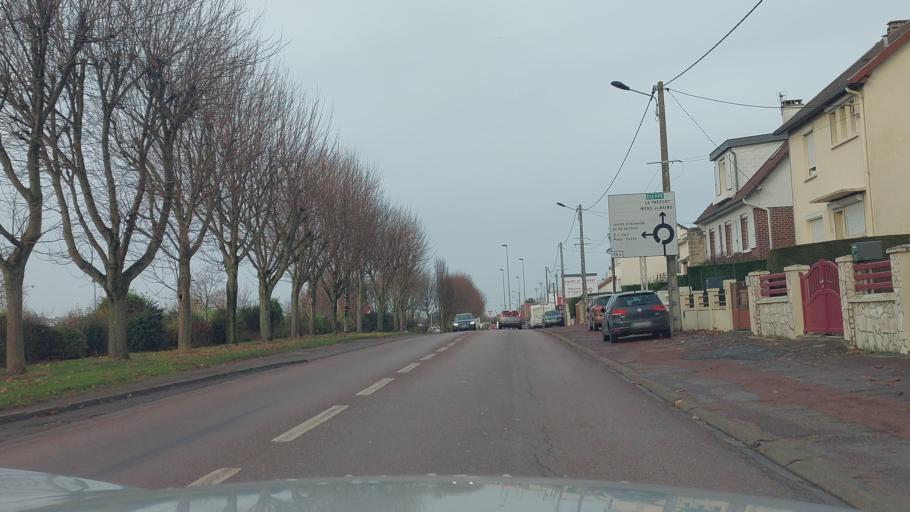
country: FR
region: Haute-Normandie
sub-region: Departement de la Seine-Maritime
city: Eu
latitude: 50.0587
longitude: 1.4173
